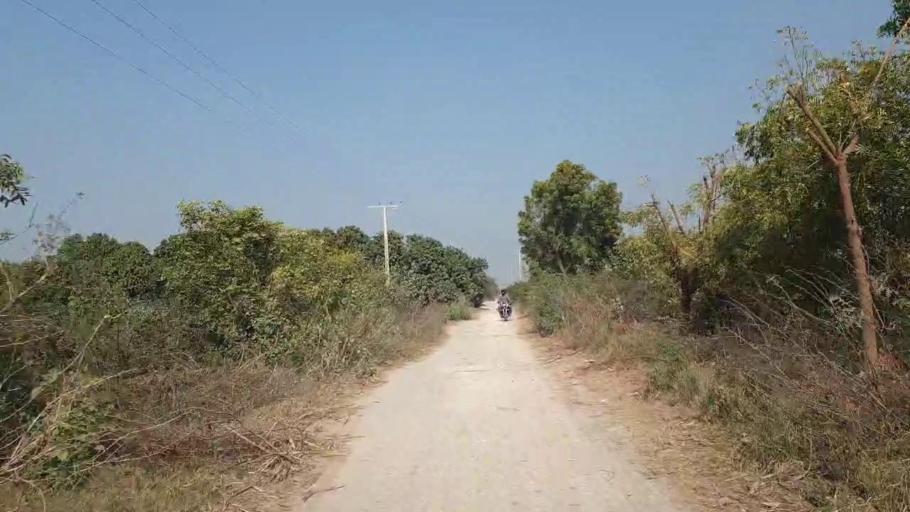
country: PK
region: Sindh
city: Chambar
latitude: 25.4038
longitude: 68.8958
